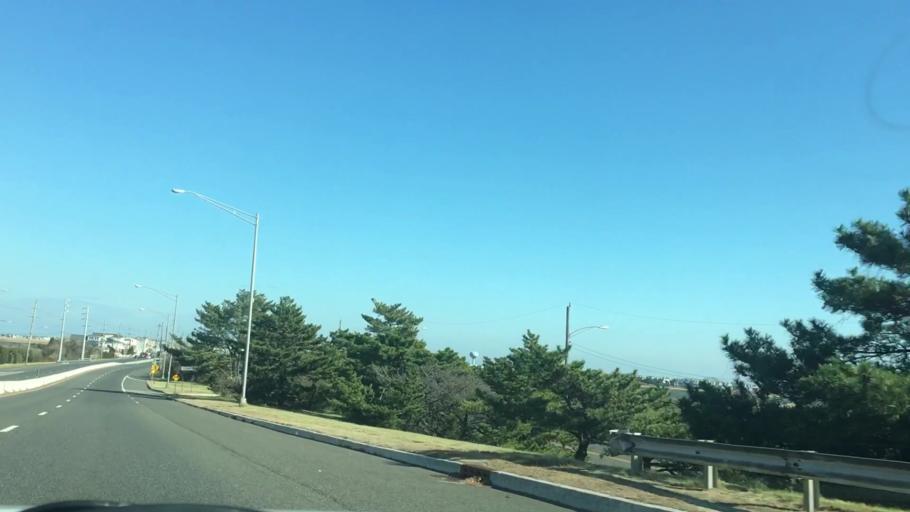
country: US
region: New Jersey
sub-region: Atlantic County
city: Atlantic City
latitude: 39.3873
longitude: -74.4184
